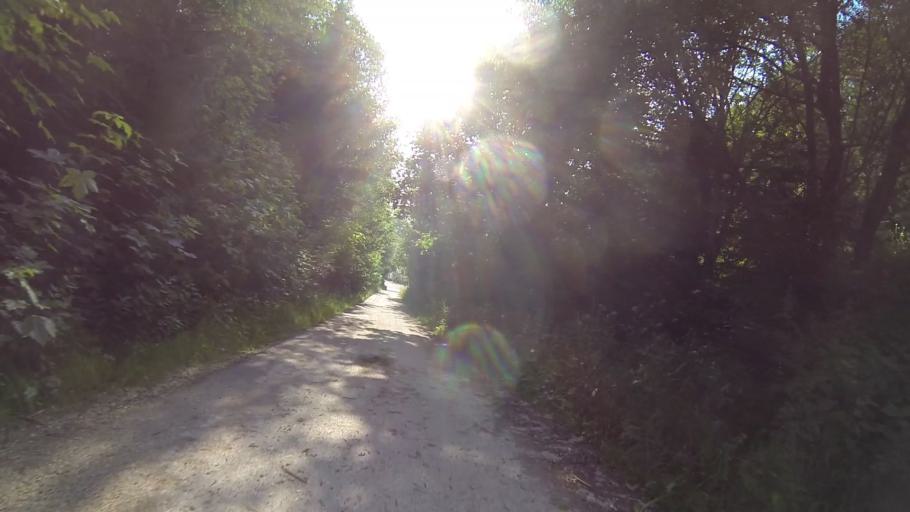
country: DE
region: Baden-Wuerttemberg
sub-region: Regierungsbezirk Stuttgart
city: Nattheim
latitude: 48.7375
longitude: 10.2680
